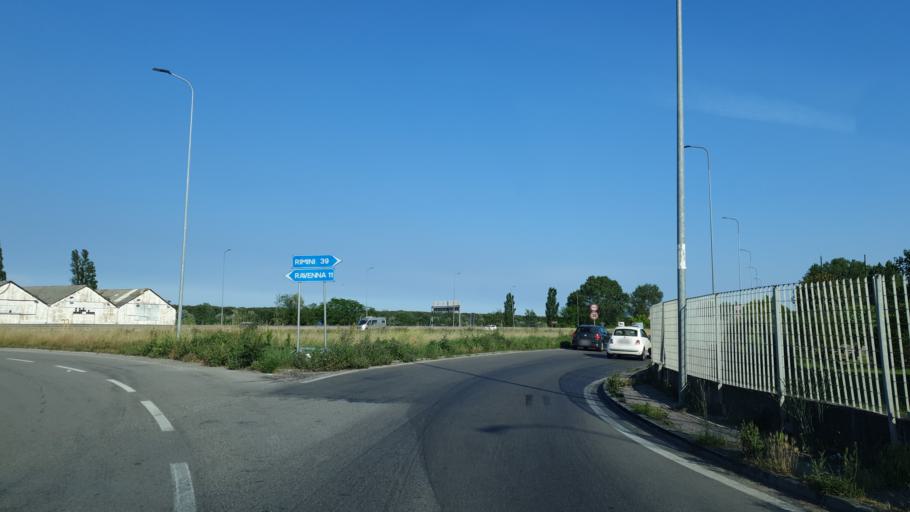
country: IT
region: Emilia-Romagna
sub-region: Provincia di Ravenna
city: Fosso Ghiaia
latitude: 44.3336
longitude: 12.2716
